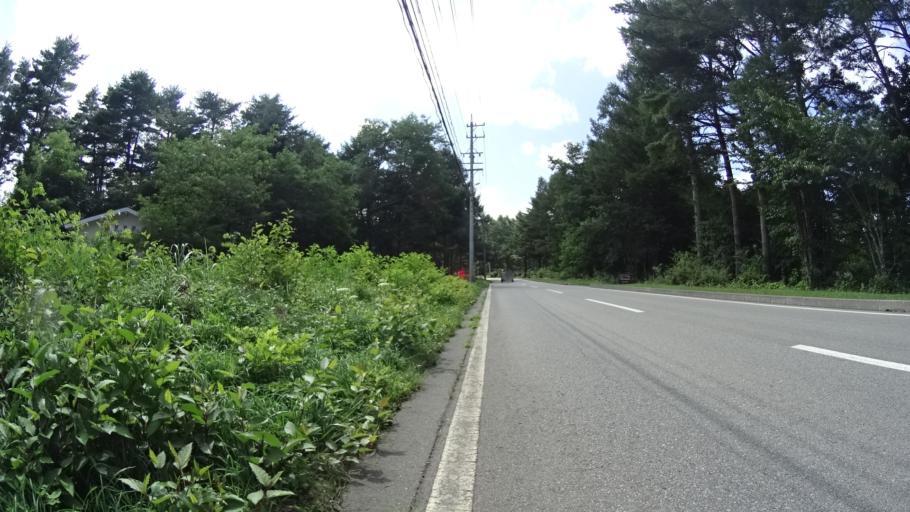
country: JP
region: Nagano
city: Saku
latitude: 36.0552
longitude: 138.4275
